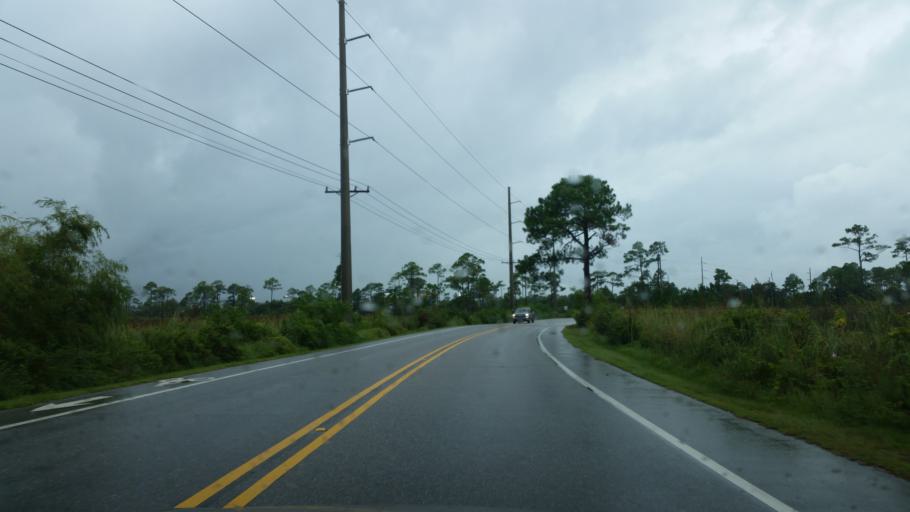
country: US
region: Alabama
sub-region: Baldwin County
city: Gulf Shores
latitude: 30.2576
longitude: -87.6806
